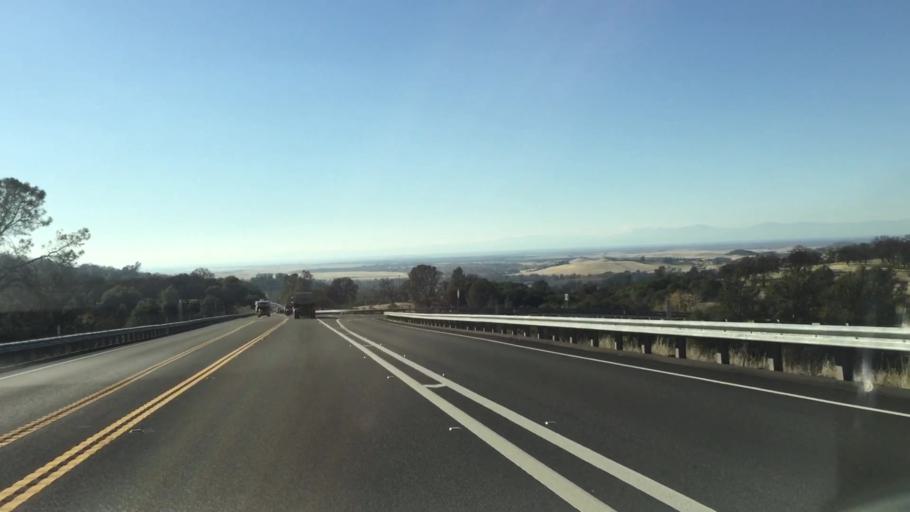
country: US
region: California
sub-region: Butte County
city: Paradise
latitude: 39.6505
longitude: -121.5585
